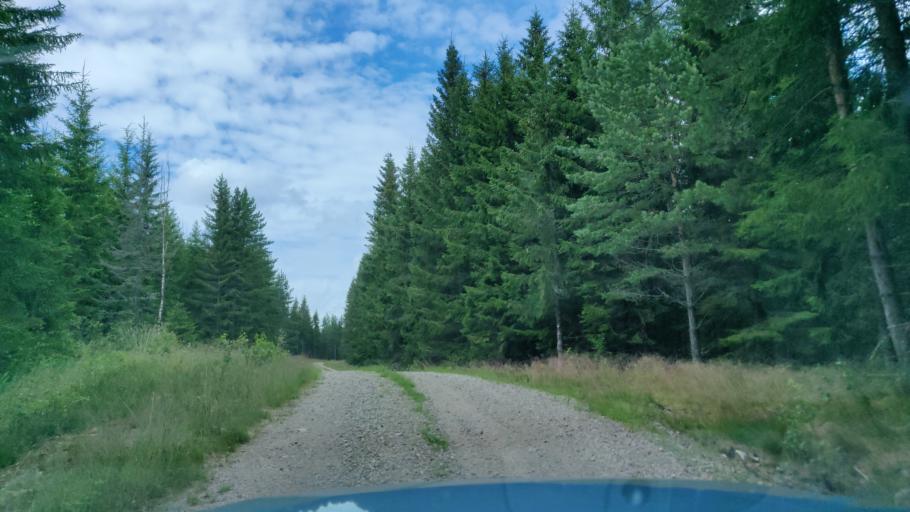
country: SE
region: Vaermland
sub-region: Hagfors Kommun
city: Hagfors
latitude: 59.9568
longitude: 13.5906
